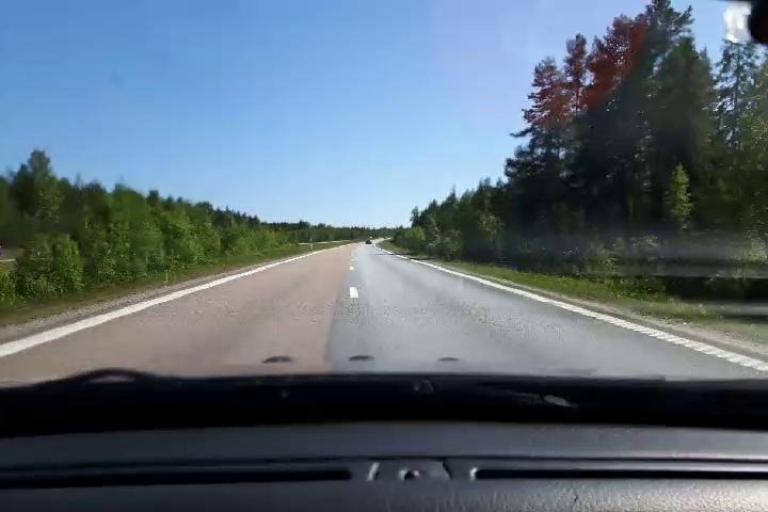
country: SE
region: Gaevleborg
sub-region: Soderhamns Kommun
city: Soderhamn
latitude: 61.4755
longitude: 16.9890
